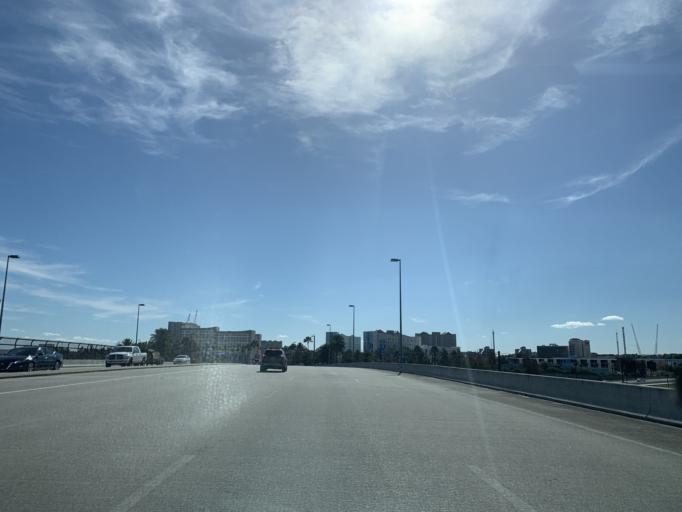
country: US
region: Florida
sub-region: Orange County
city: Tangelo Park
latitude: 28.4668
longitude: -81.4651
